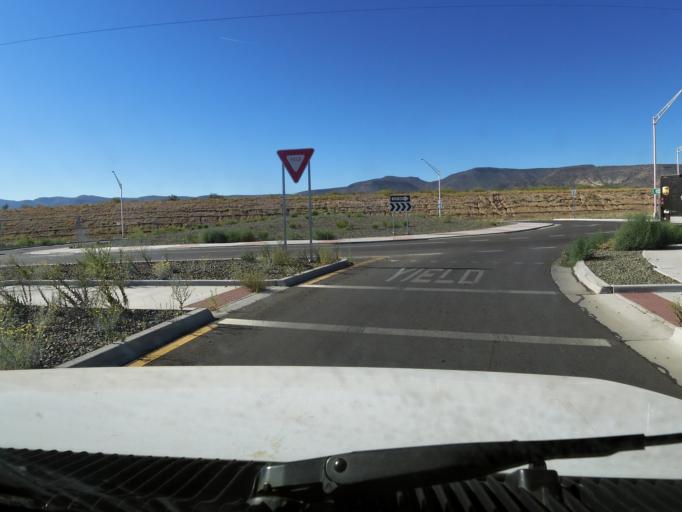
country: US
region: Arizona
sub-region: Yavapai County
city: Camp Verde
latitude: 34.5989
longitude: -111.8973
